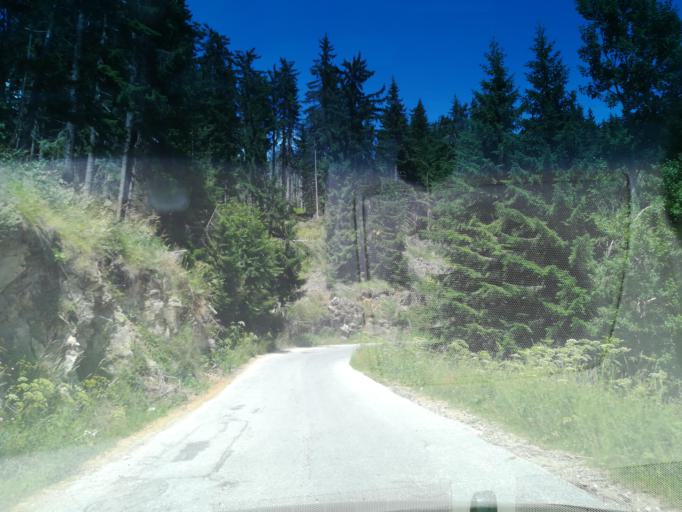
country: BG
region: Smolyan
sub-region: Obshtina Chepelare
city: Chepelare
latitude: 41.6915
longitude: 24.7707
